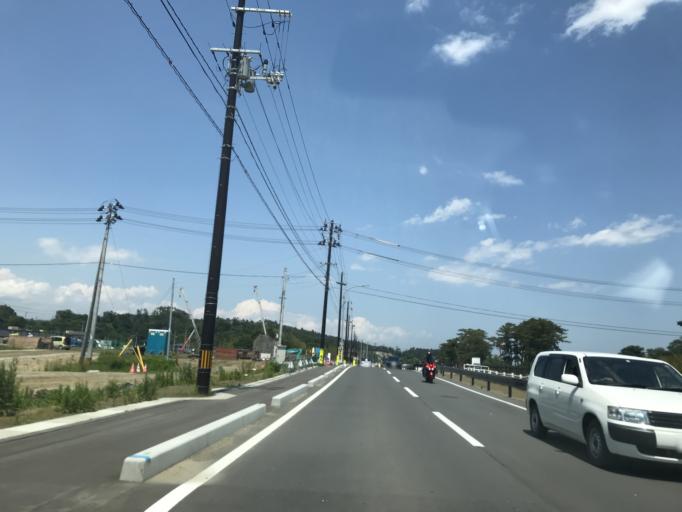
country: JP
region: Miyagi
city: Yamoto
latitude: 38.3712
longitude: 141.1515
